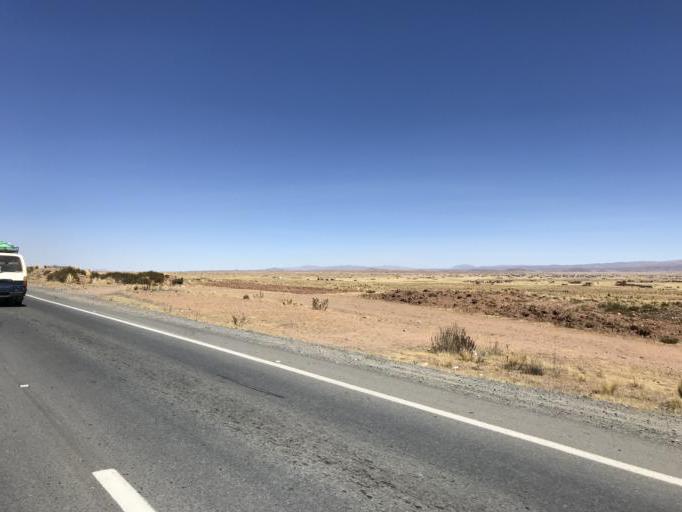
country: BO
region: La Paz
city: Batallas
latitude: -16.3996
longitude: -68.3599
